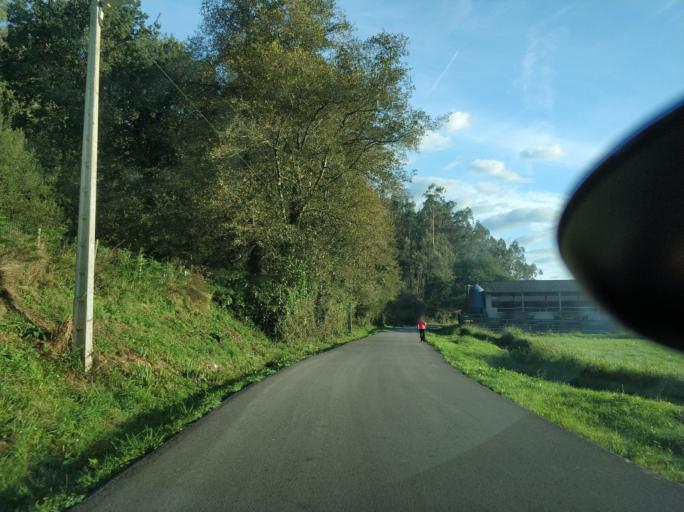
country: ES
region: Cantabria
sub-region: Provincia de Cantabria
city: Polanco
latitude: 43.3630
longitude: -3.9697
